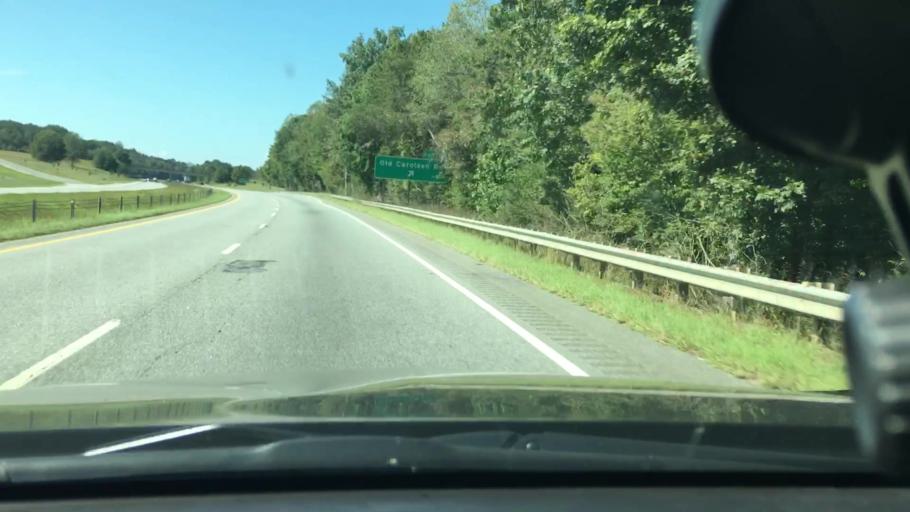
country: US
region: North Carolina
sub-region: Rutherford County
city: Forest City
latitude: 35.3196
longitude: -81.8247
